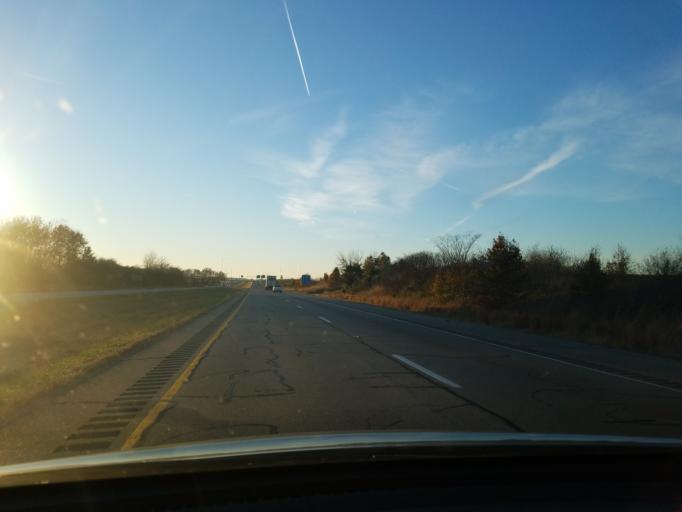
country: US
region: Indiana
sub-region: Gibson County
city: Haubstadt
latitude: 38.1671
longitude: -87.5373
